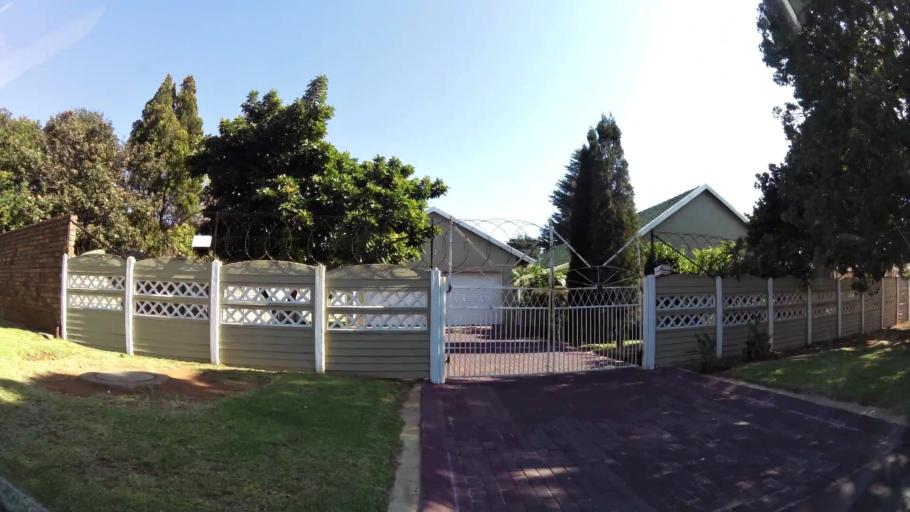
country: ZA
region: Gauteng
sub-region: Ekurhuleni Metropolitan Municipality
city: Tembisa
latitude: -26.0434
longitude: 28.2097
